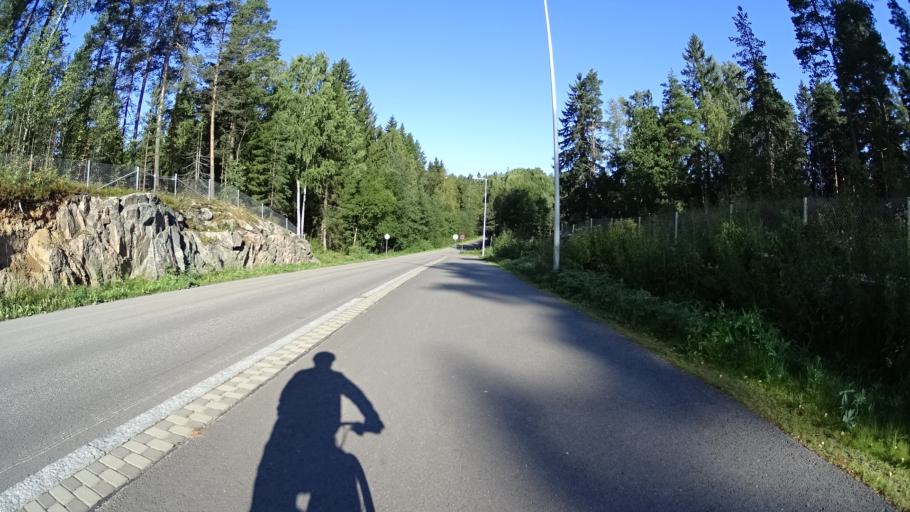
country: FI
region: Uusimaa
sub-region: Helsinki
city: Kilo
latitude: 60.2567
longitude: 24.7927
